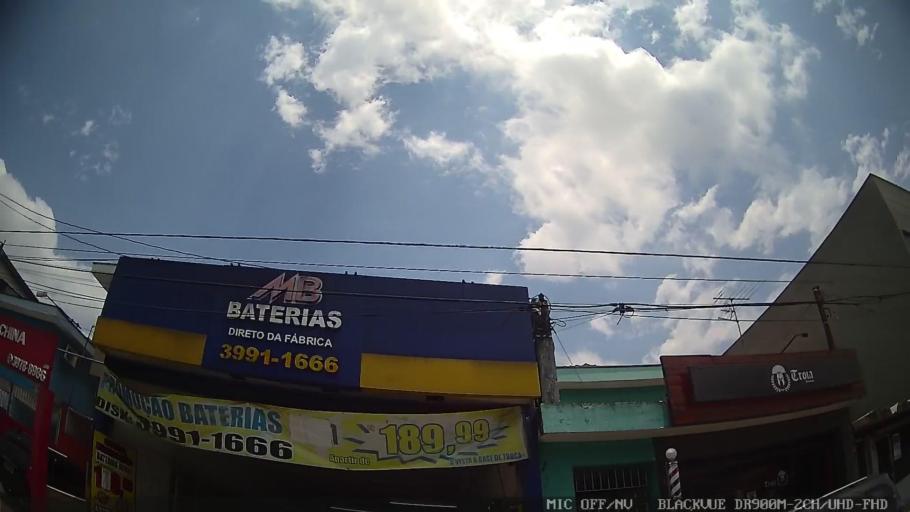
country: BR
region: Sao Paulo
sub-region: Osasco
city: Osasco
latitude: -23.4863
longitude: -46.7154
